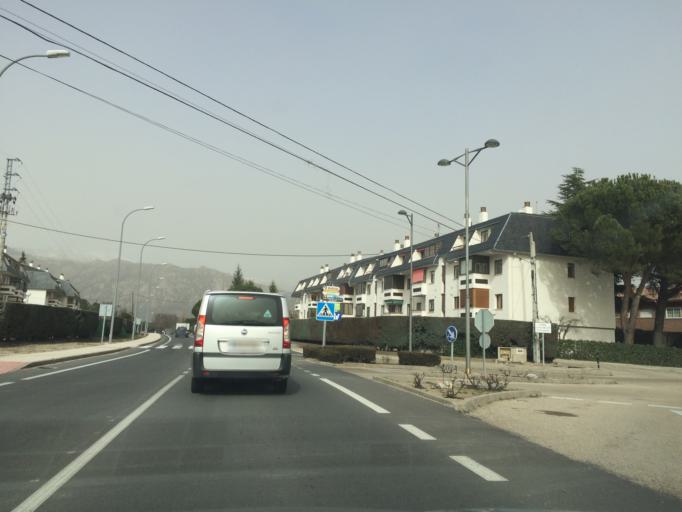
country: ES
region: Madrid
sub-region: Provincia de Madrid
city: Boalo
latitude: 40.6969
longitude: -3.9378
